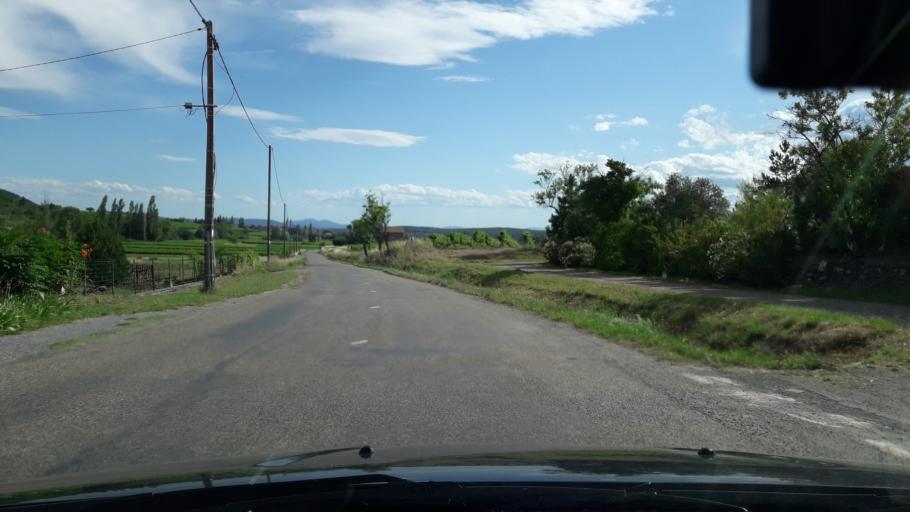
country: FR
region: Rhone-Alpes
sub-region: Departement de l'Ardeche
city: Vesseaux
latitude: 44.6230
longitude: 4.4806
